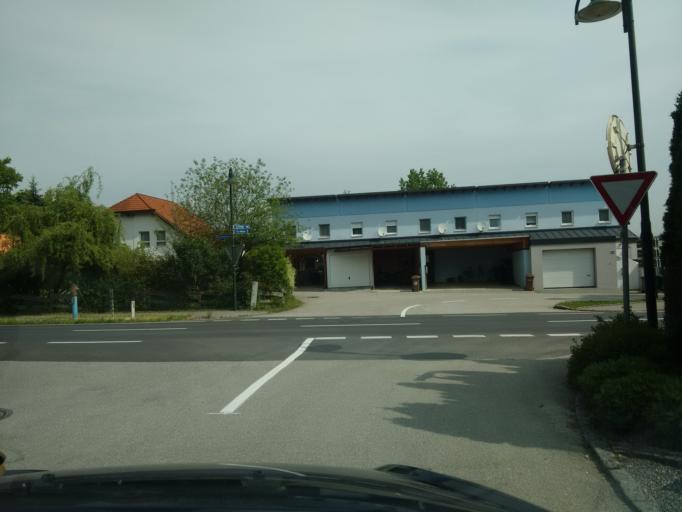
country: AT
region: Upper Austria
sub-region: Wels-Land
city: Marchtrenk
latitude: 48.1618
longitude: 14.0914
